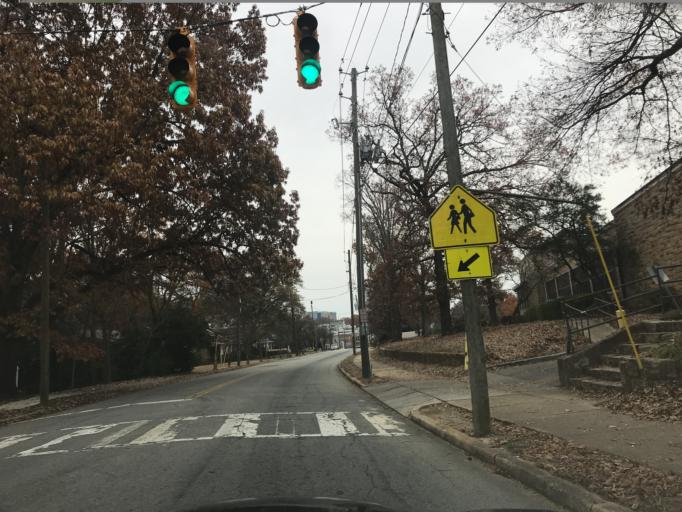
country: US
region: North Carolina
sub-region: Wake County
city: West Raleigh
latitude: 35.7909
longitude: -78.6516
